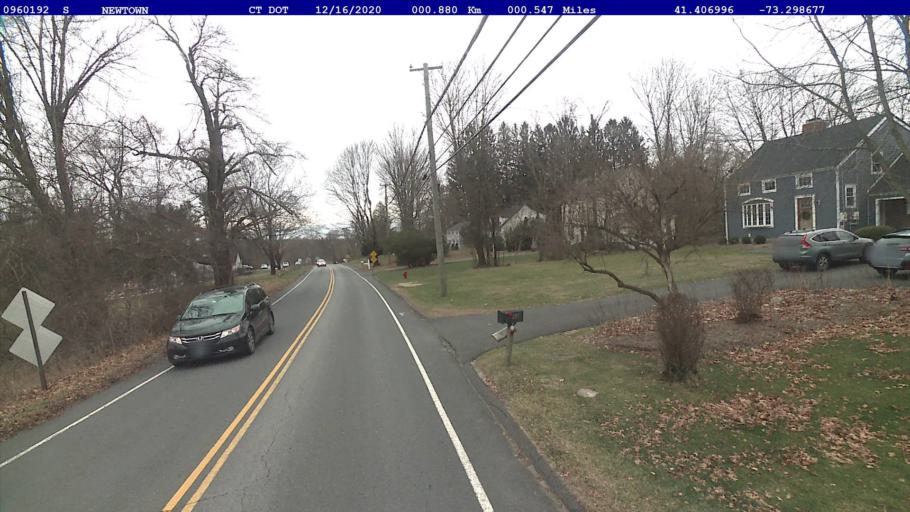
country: US
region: Connecticut
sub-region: Fairfield County
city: Newtown
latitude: 41.4070
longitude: -73.2987
